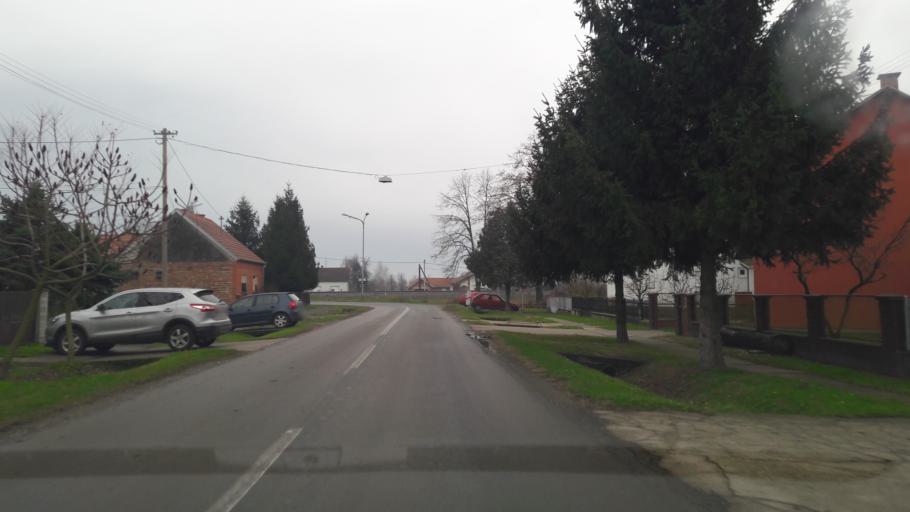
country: HR
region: Osjecko-Baranjska
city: Koska
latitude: 45.5420
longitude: 18.2917
